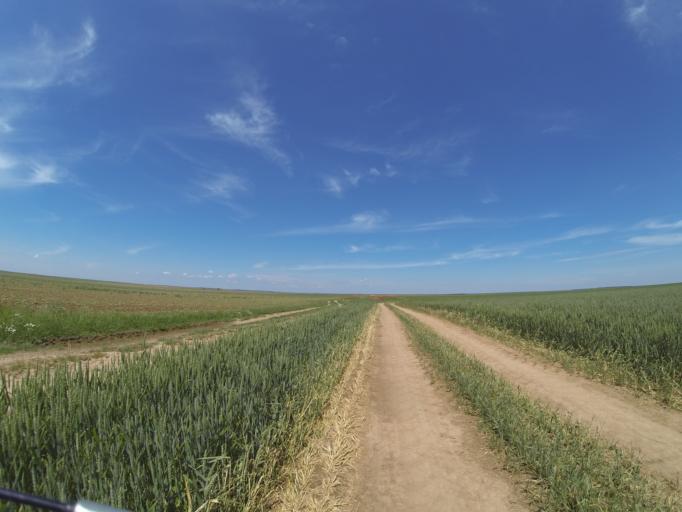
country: RO
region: Dolj
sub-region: Comuna Teslui
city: Teslui
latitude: 44.1813
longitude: 24.1713
